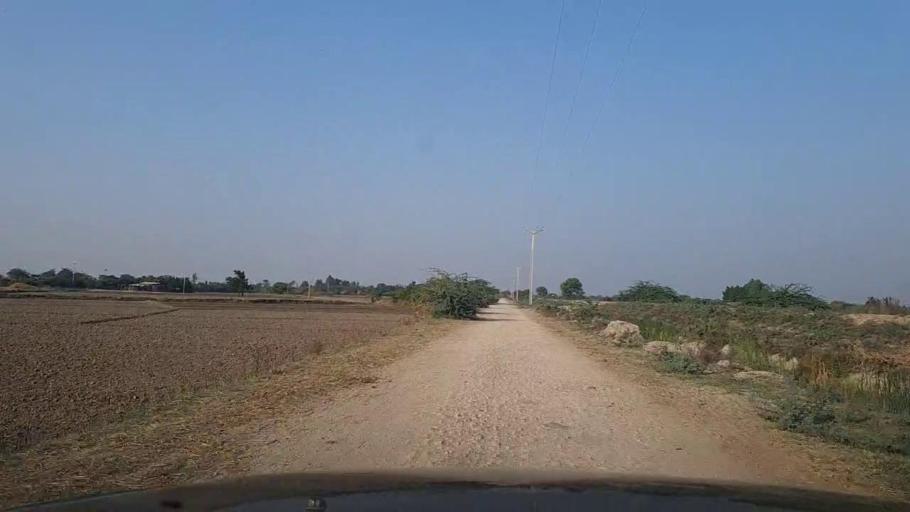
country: PK
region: Sindh
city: Thatta
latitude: 24.7508
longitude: 67.9588
